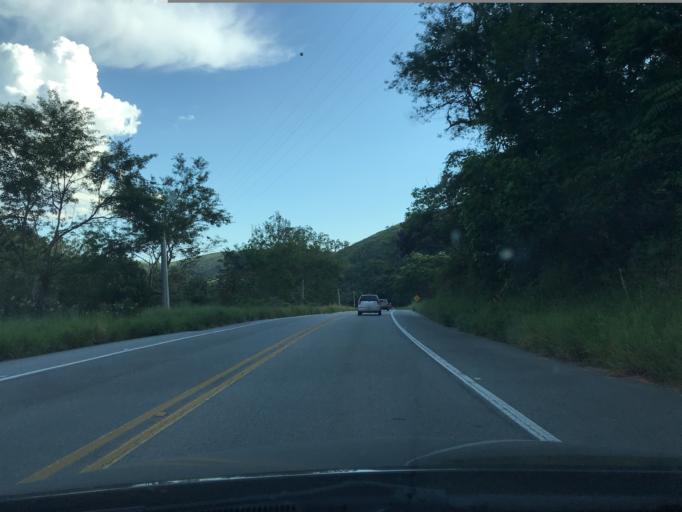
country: BR
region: Sao Paulo
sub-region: Tremembe
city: Tremembe
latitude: -22.8836
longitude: -45.5972
